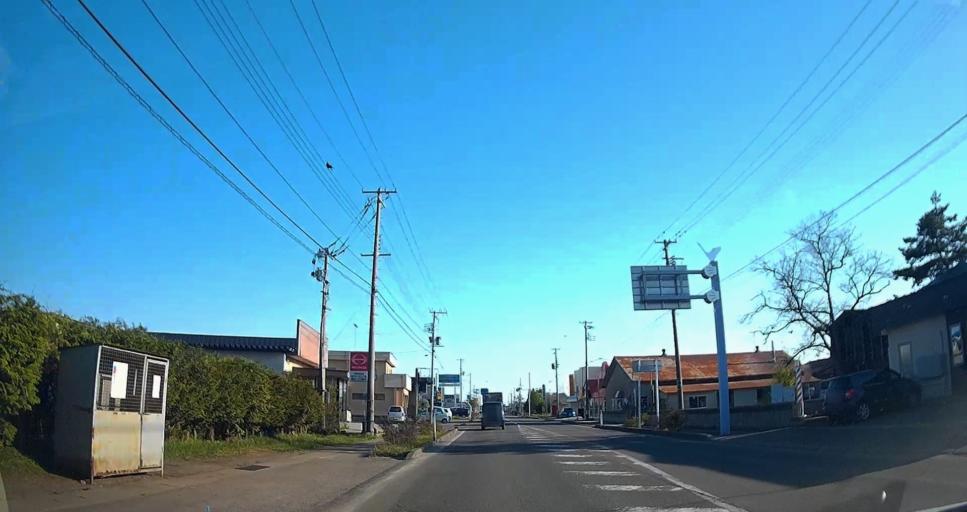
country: JP
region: Aomori
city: Mutsu
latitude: 41.2966
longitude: 141.2213
